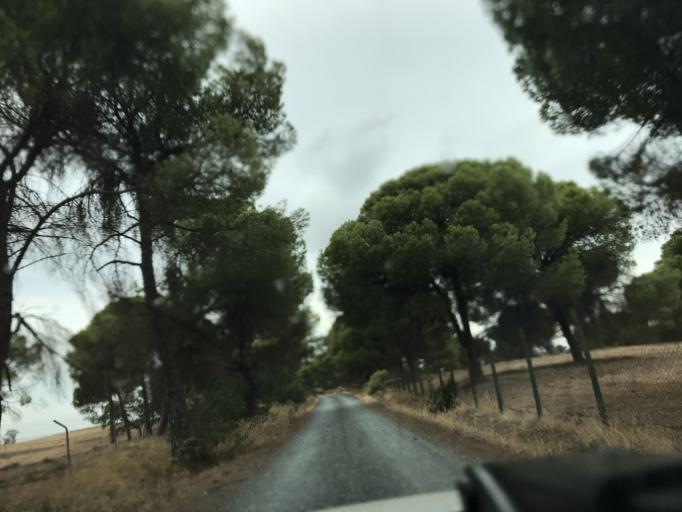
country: ES
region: Andalusia
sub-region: Provincia de Sevilla
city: Villanueva del Rio y Minas
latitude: 37.6719
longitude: -5.7341
